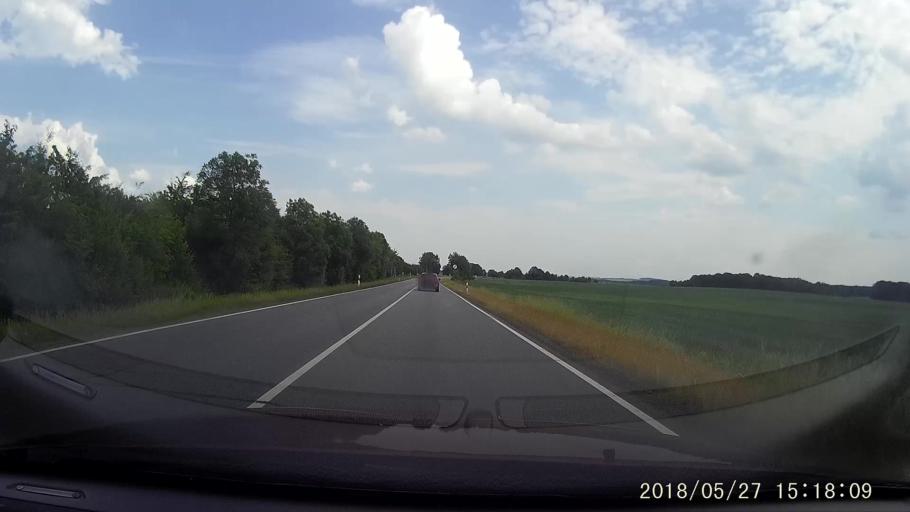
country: DE
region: Saxony
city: Niesky
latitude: 51.2672
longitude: 14.8524
